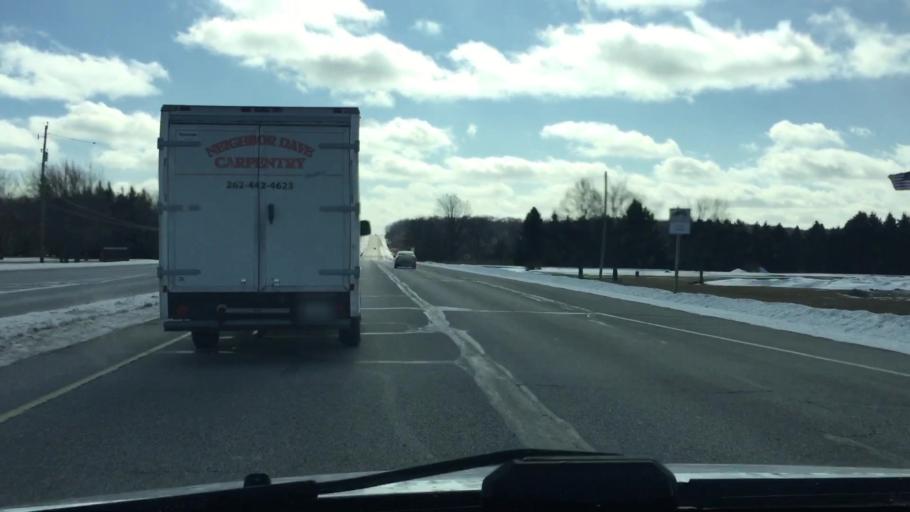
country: US
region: Wisconsin
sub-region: Waukesha County
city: Waukesha
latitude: 42.9481
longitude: -88.2283
